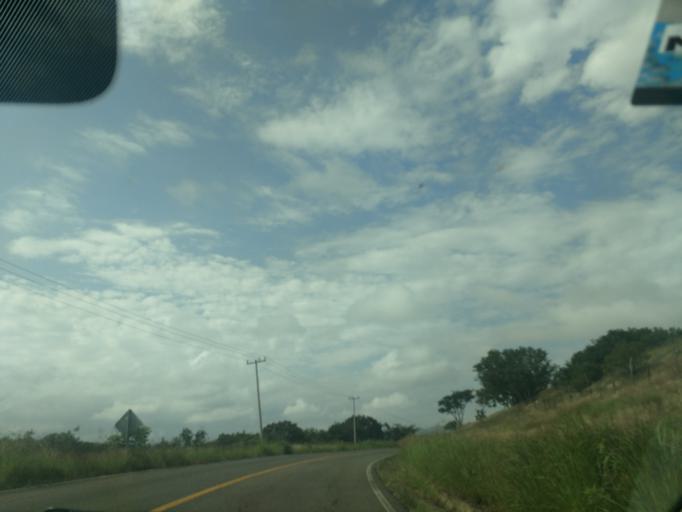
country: MX
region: Jalisco
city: El Salto
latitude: 20.3910
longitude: -104.5248
